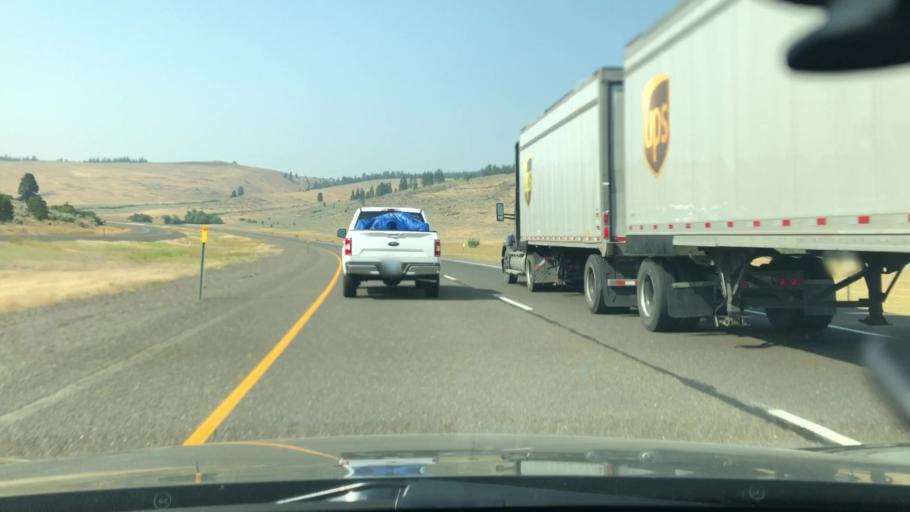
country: US
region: Oregon
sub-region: Union County
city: Union
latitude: 45.1605
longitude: -117.9642
